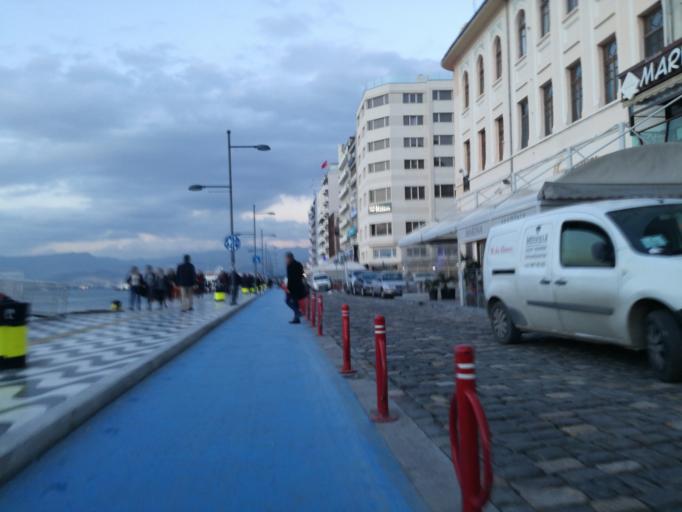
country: TR
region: Izmir
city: Izmir
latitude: 38.4256
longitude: 27.1318
